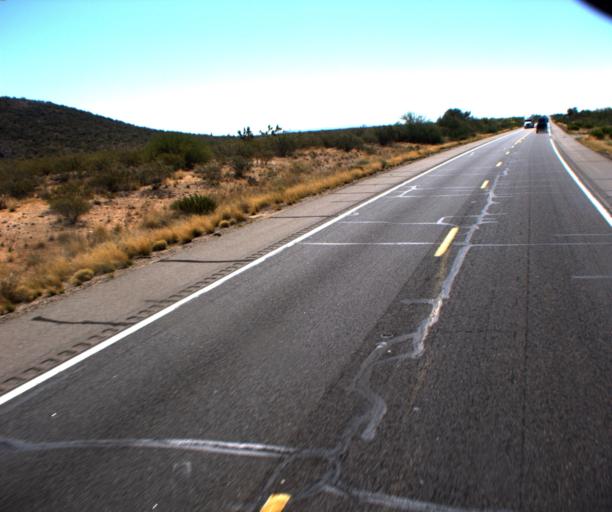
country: US
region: Arizona
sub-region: Yavapai County
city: Congress
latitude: 34.1731
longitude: -113.0221
